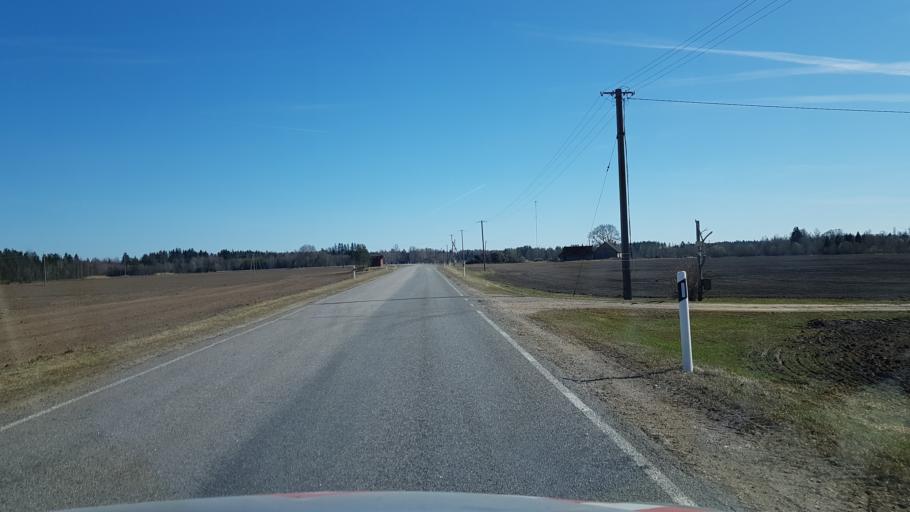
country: EE
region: Laeaene-Virumaa
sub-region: Vinni vald
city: Vinni
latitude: 59.2391
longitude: 26.6931
